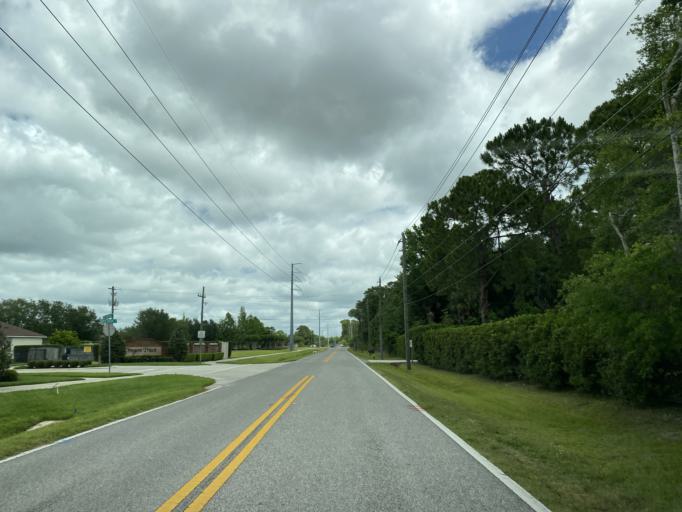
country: US
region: Florida
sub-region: Volusia County
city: DeBary
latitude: 28.8252
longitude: -81.3393
